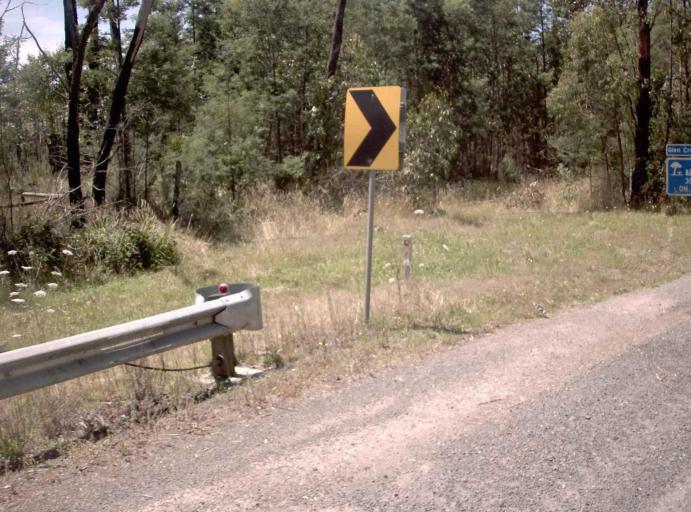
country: AU
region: Victoria
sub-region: Baw Baw
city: Warragul
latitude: -38.0732
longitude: 145.8901
